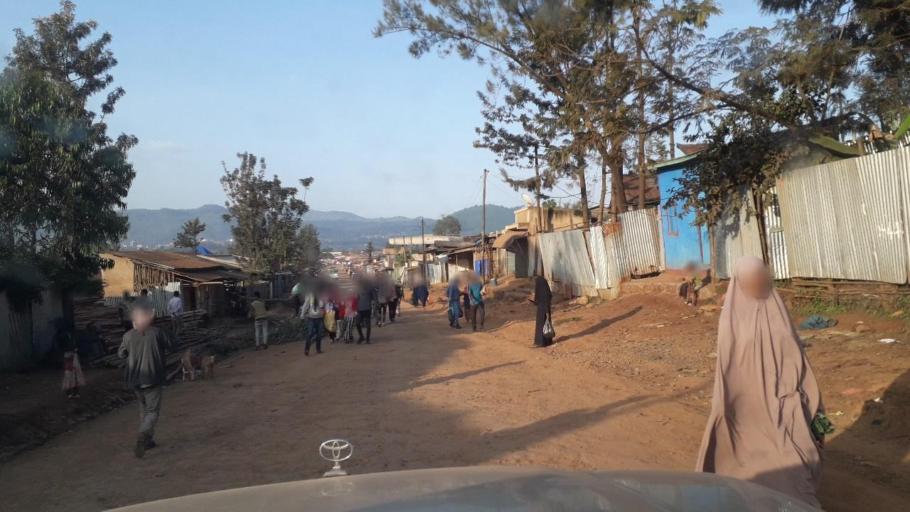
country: ET
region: Oromiya
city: Jima
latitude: 7.6408
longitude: 36.8418
